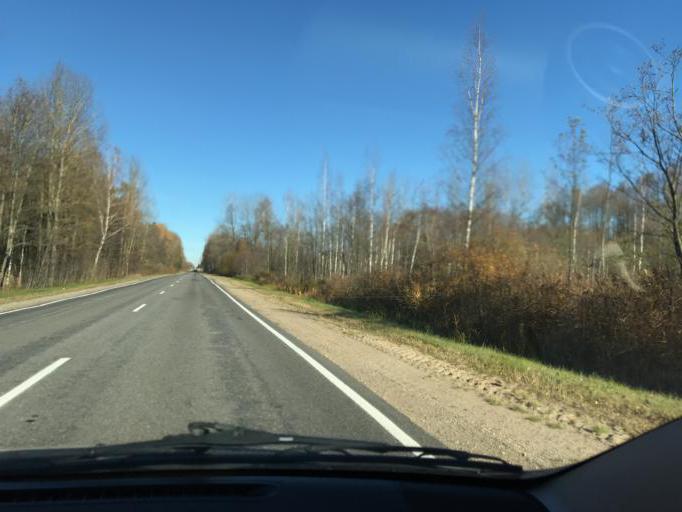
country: BY
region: Vitebsk
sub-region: Ushatski Rayon
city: Ushachy
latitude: 55.0749
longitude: 28.7545
